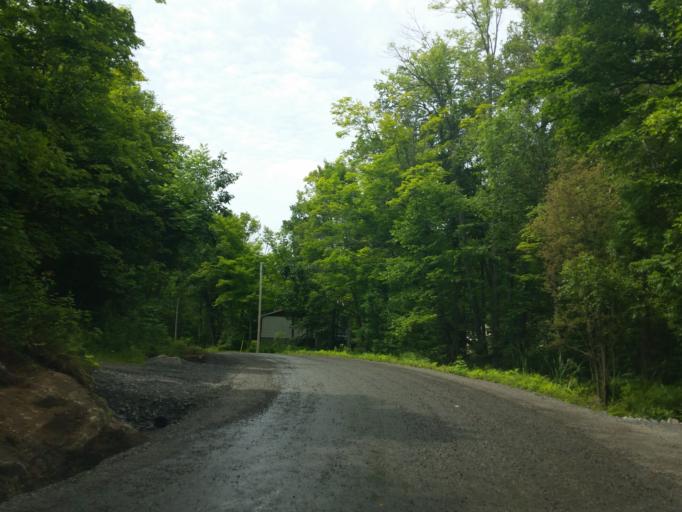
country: CA
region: Ontario
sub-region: Parry Sound District
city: Parry Sound
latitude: 45.4368
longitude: -80.0024
